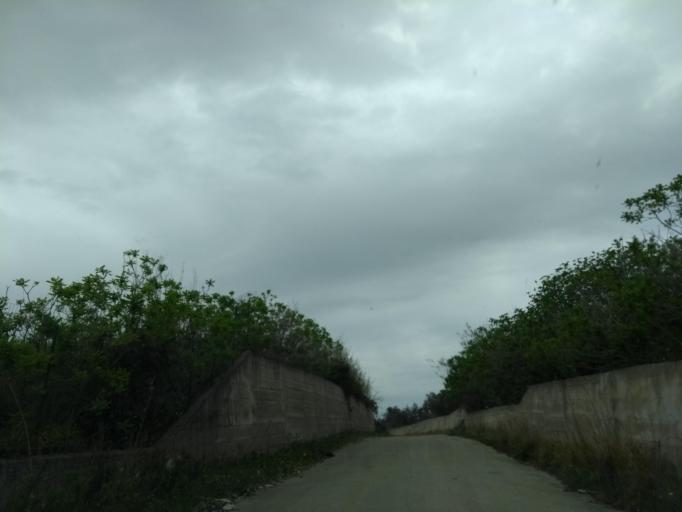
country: IT
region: Sicily
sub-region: Palermo
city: Partinico
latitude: 37.9944
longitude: 13.0801
